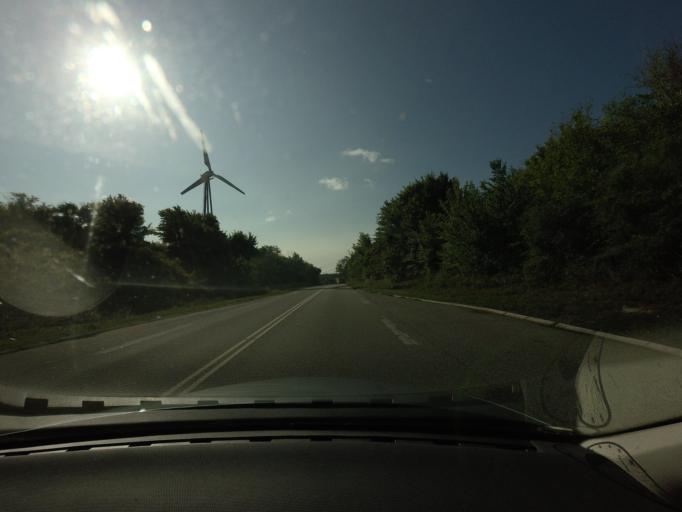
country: DK
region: Zealand
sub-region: Vordingborg Kommune
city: Praesto
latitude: 55.1068
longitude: 12.0687
